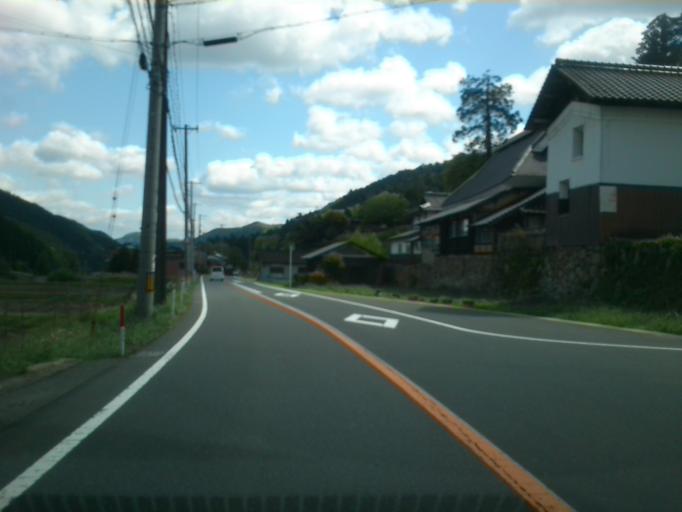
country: JP
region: Kyoto
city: Fukuchiyama
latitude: 35.3751
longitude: 135.0452
